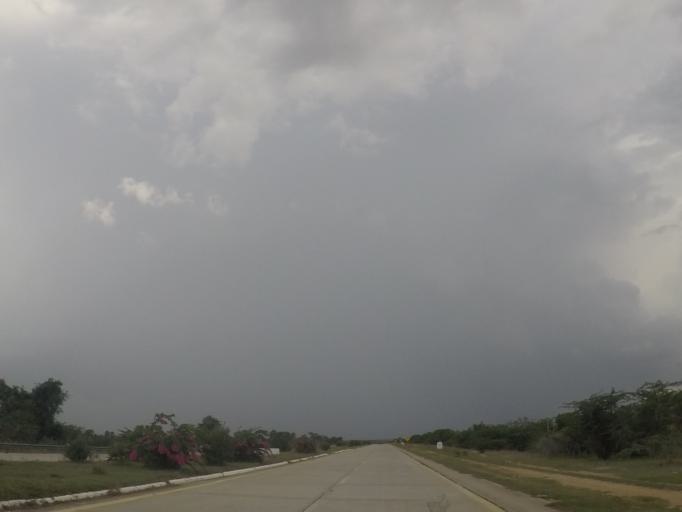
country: MM
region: Mandalay
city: Meiktila
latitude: 21.0624
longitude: 95.7880
